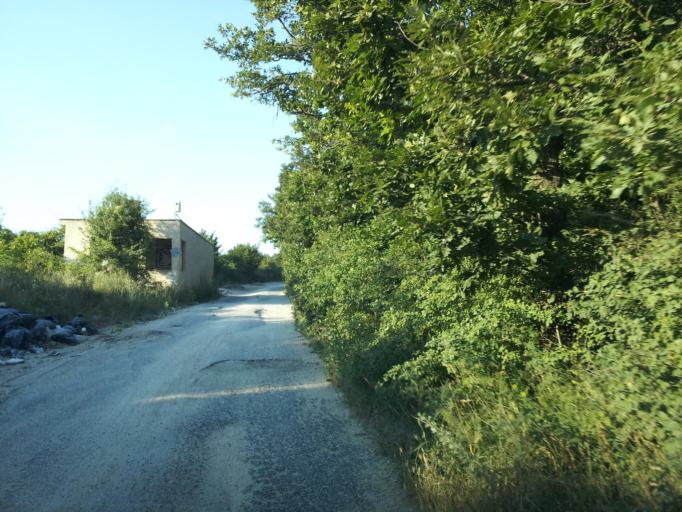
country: HU
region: Veszprem
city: Szentkiralyszabadja
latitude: 47.0621
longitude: 17.9905
